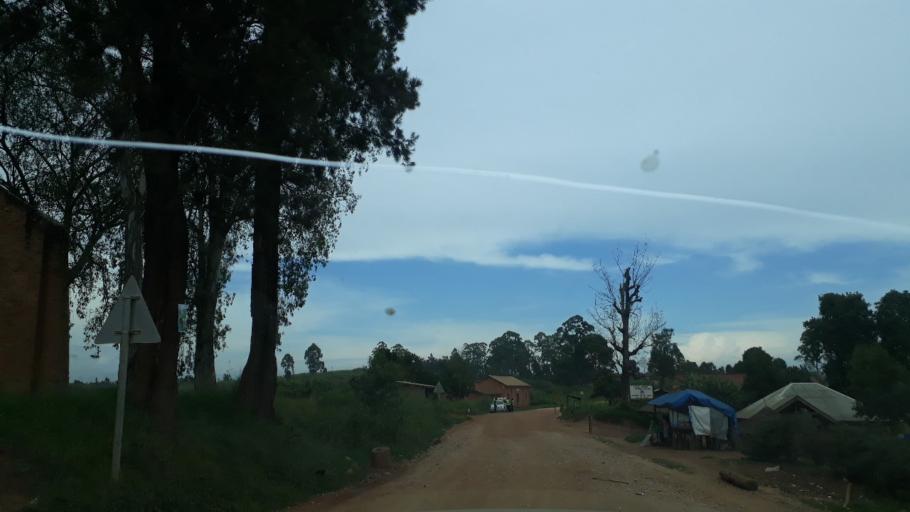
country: CD
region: Eastern Province
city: Bunia
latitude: 1.9199
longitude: 30.5025
